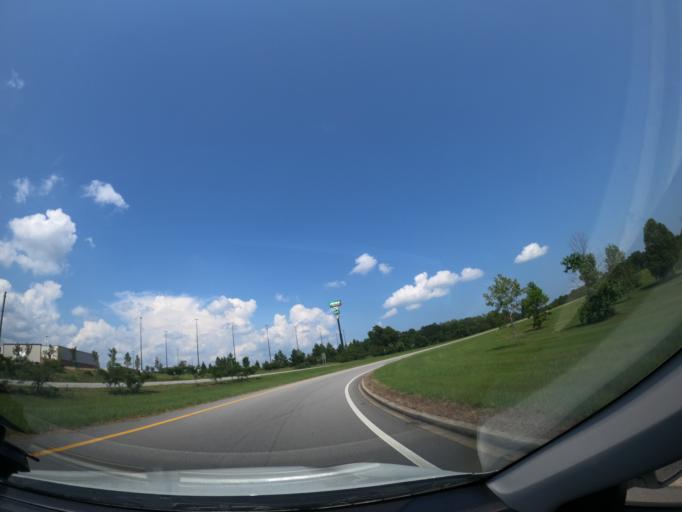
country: US
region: South Carolina
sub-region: Richland County
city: Columbia
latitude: 33.9515
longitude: -80.9902
